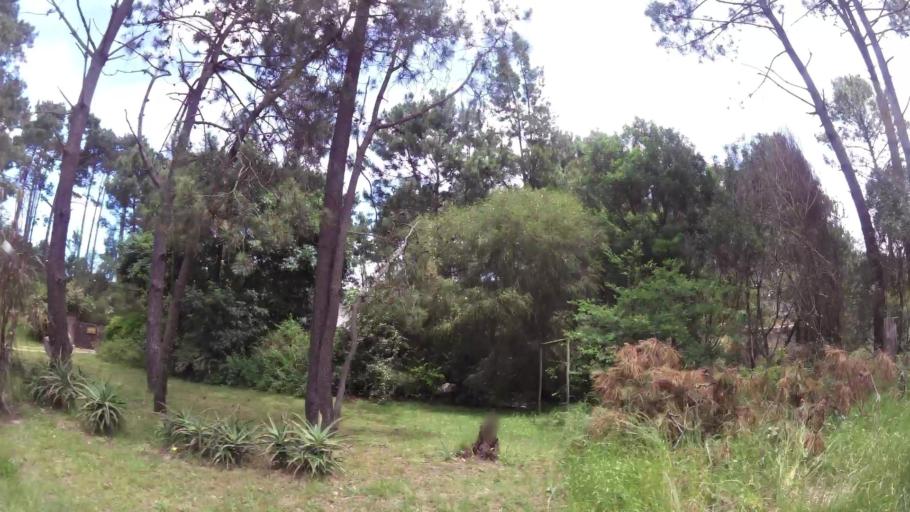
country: UY
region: Canelones
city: Empalme Olmos
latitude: -34.7949
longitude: -55.8932
